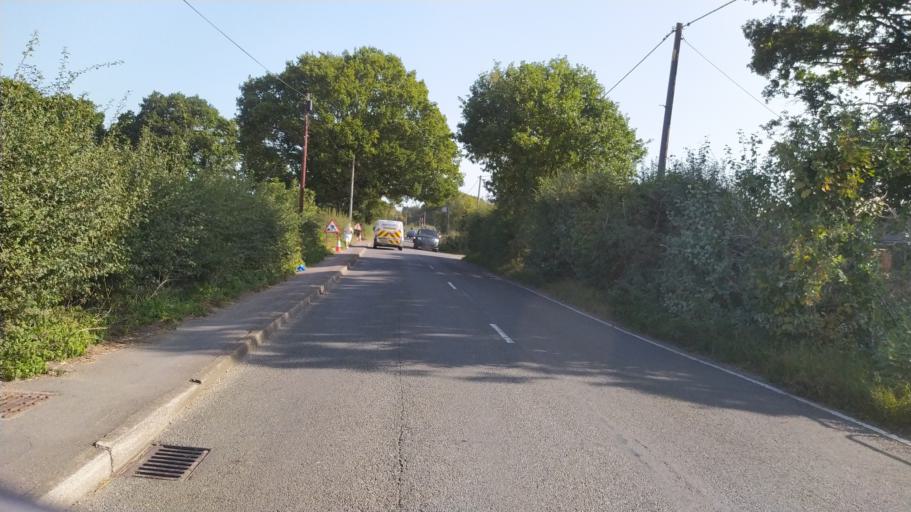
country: GB
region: England
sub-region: Hampshire
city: Botley
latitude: 50.9214
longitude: -1.2832
